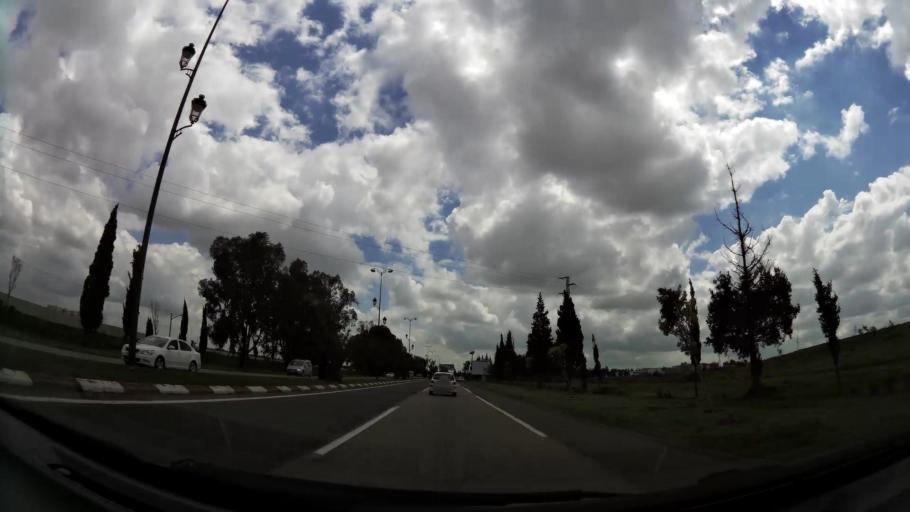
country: MA
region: Chaouia-Ouardigha
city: Nouaseur
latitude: 33.3880
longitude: -7.5656
